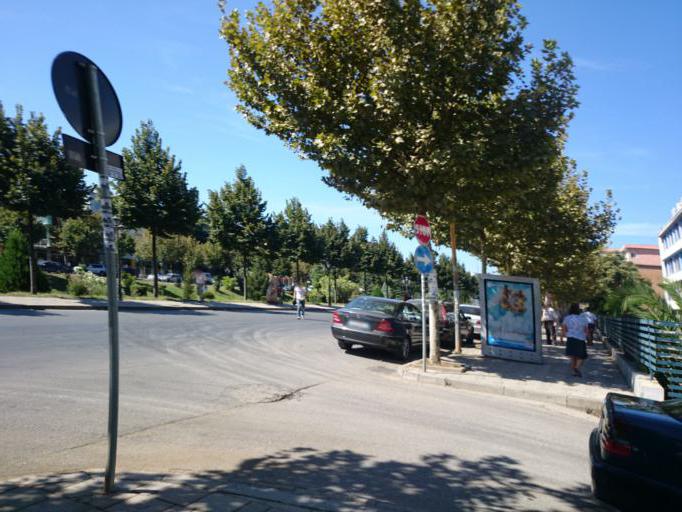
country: AL
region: Tirane
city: Tirana
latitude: 41.3215
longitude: 19.8034
